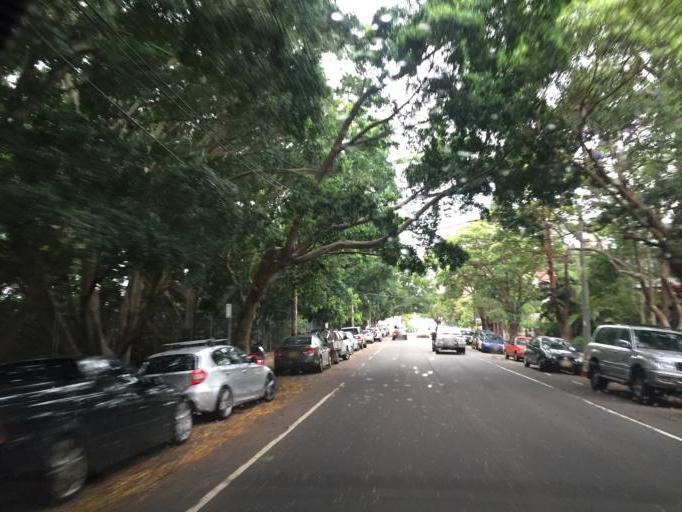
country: AU
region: New South Wales
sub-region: Waverley
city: Bondi Beach
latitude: -33.8840
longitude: 151.2663
